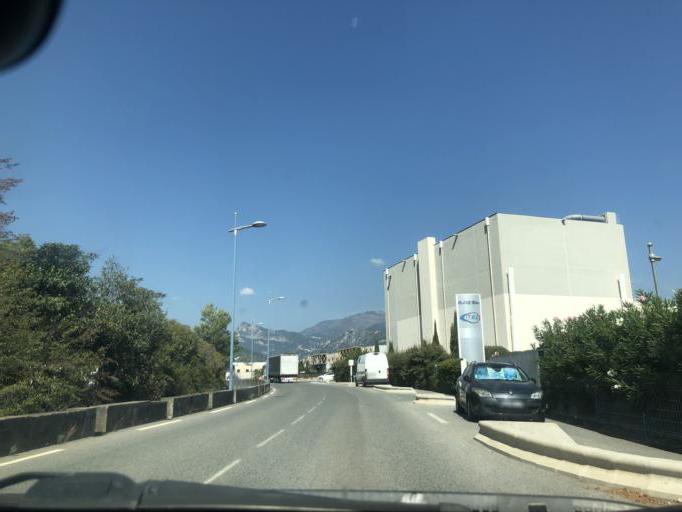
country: FR
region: Provence-Alpes-Cote d'Azur
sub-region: Departement des Alpes-Maritimes
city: Carros
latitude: 43.7978
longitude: 7.1972
